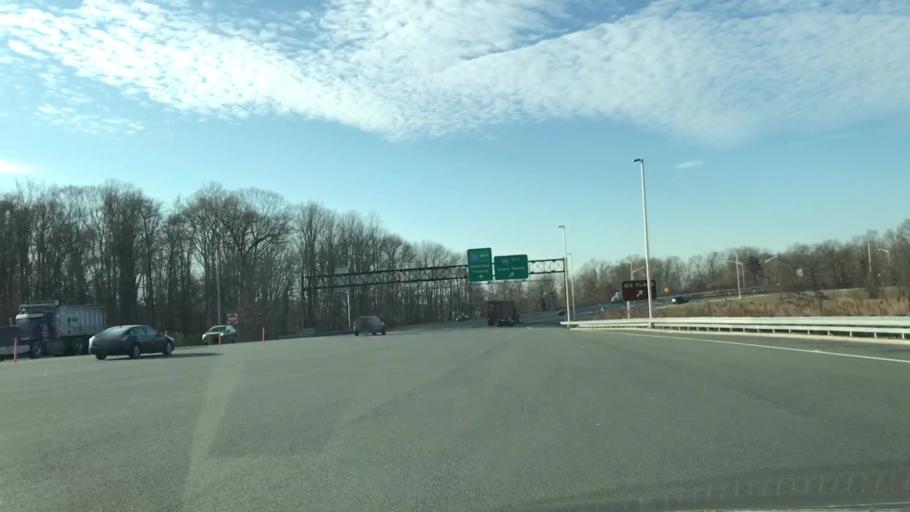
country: US
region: New Jersey
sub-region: Mercer County
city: Robbinsville
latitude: 40.1946
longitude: -74.6081
